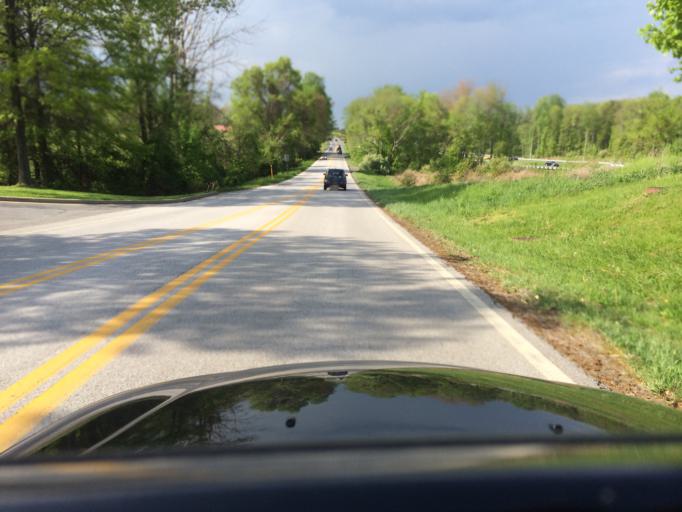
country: US
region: Maryland
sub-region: Howard County
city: Highland
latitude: 39.2665
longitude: -76.9866
